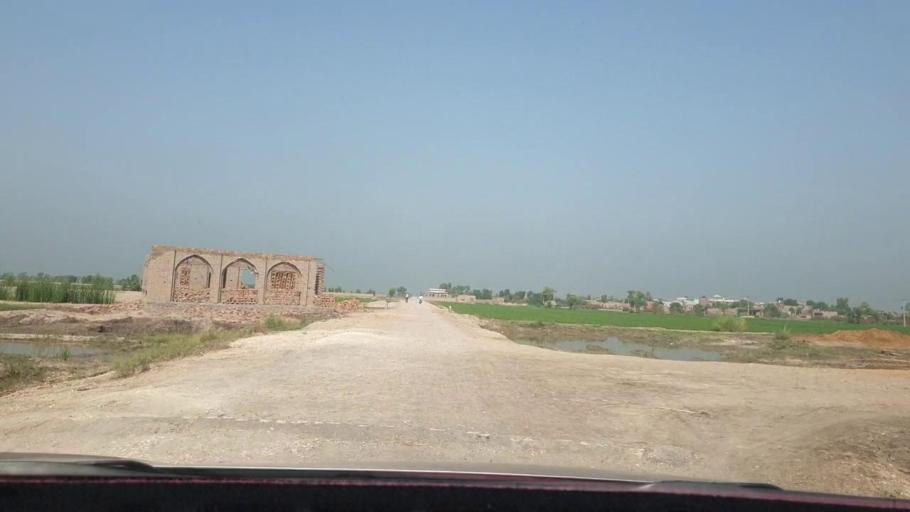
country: PK
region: Sindh
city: Nasirabad
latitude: 27.4355
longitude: 67.9610
